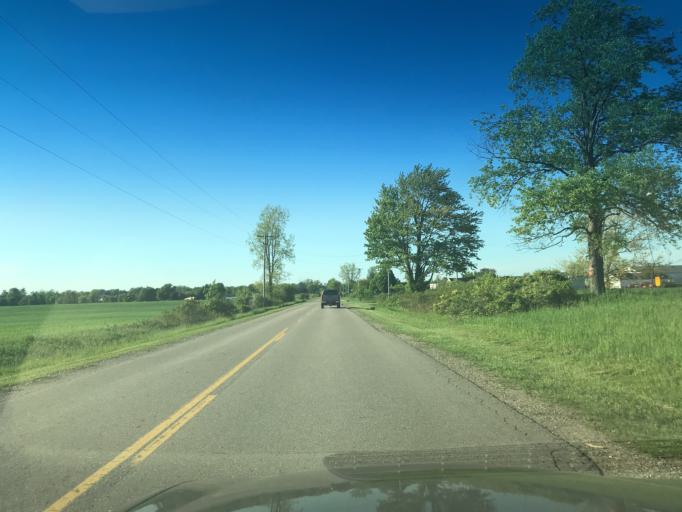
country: US
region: Michigan
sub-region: Ingham County
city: Mason
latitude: 42.5617
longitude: -84.4530
